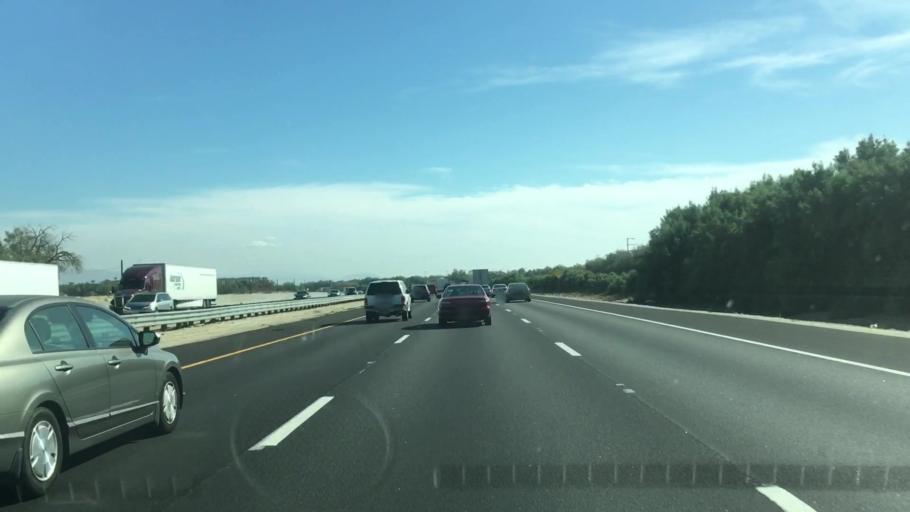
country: US
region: California
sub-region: Riverside County
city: Bermuda Dunes
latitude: 33.7673
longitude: -116.3239
